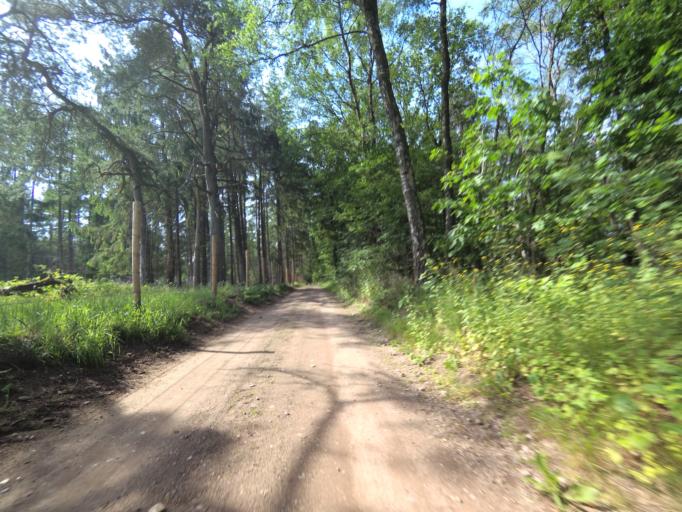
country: NL
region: Gelderland
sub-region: Gemeente Apeldoorn
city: Beekbergen
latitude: 52.1121
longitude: 5.8832
